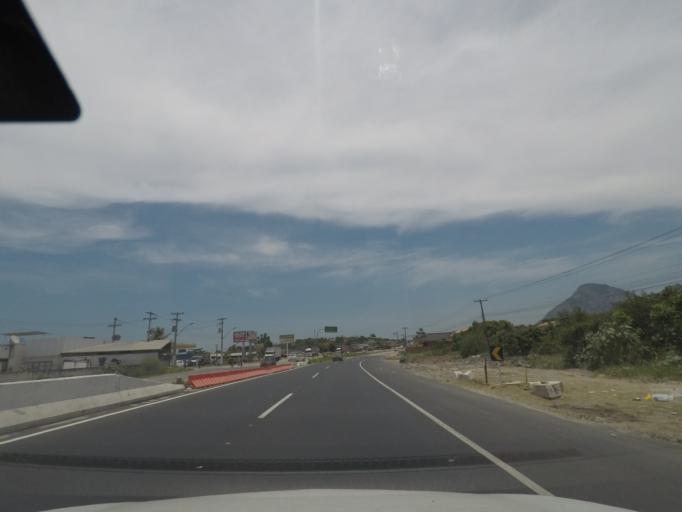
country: BR
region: Rio de Janeiro
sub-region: Marica
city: Marica
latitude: -22.9295
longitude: -42.8714
